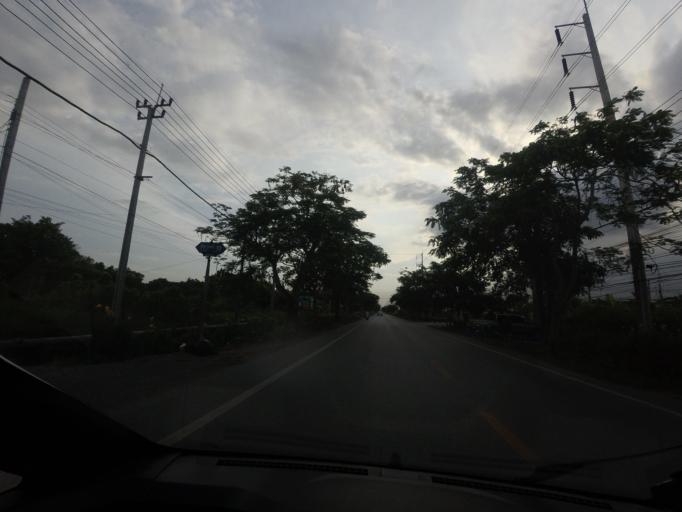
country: TH
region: Bangkok
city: Nong Chok
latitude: 13.8582
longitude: 100.8410
